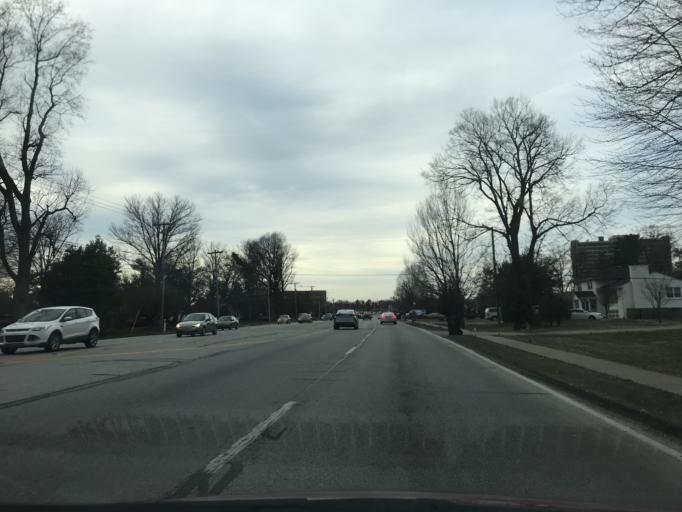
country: US
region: Kentucky
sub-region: Jefferson County
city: West Buechel
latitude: 38.1973
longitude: -85.6814
